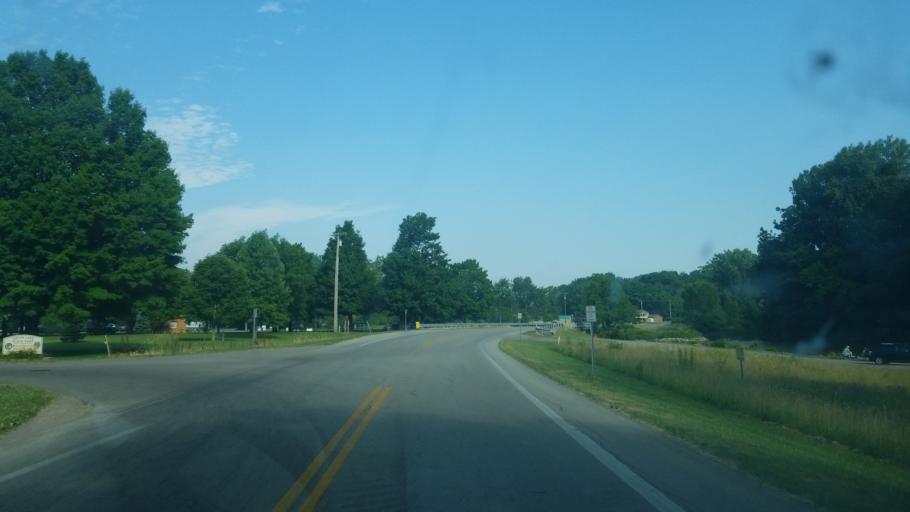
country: US
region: Ohio
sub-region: Logan County
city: Russells Point
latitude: 40.4785
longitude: -83.8587
